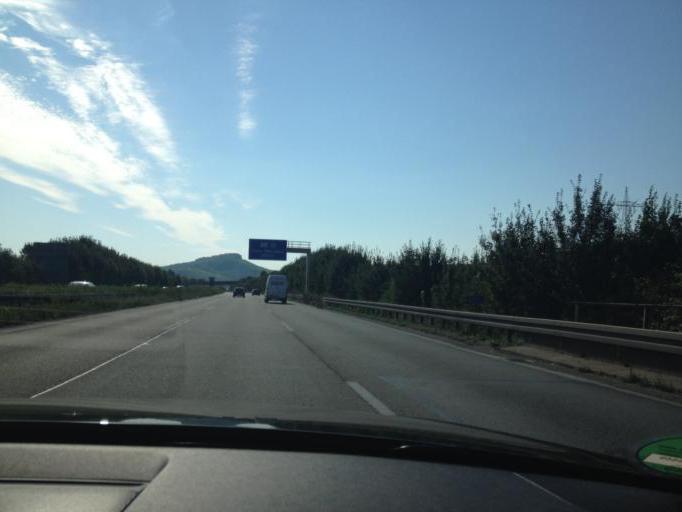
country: DE
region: Baden-Wuerttemberg
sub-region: Regierungsbezirk Stuttgart
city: Erlenbach
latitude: 49.1732
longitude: 9.2454
